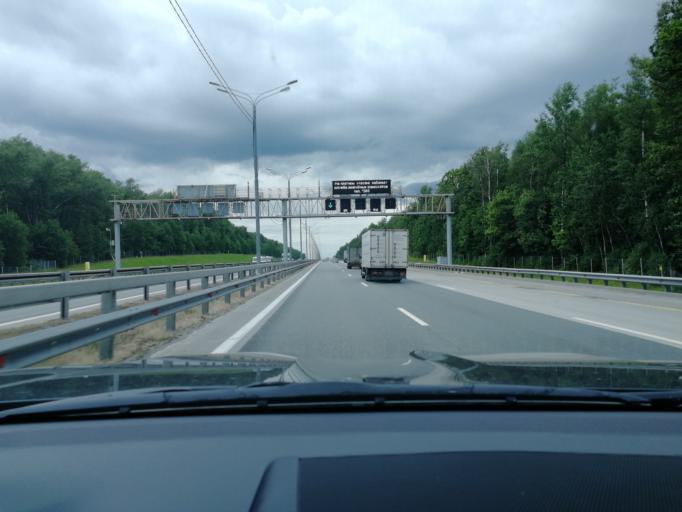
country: RU
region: Moskovskaya
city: Belyye Stolby
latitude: 55.2941
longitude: 37.8456
